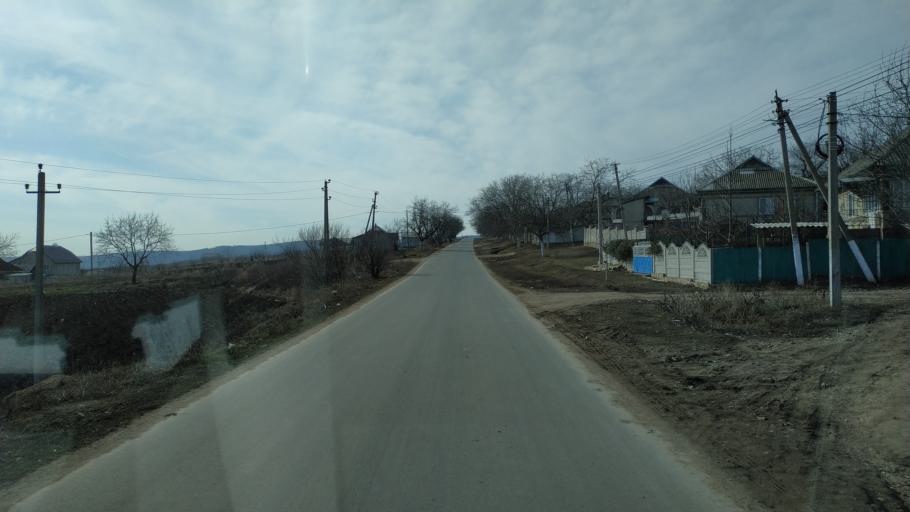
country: MD
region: Nisporeni
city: Nisporeni
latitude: 47.1502
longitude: 28.1275
